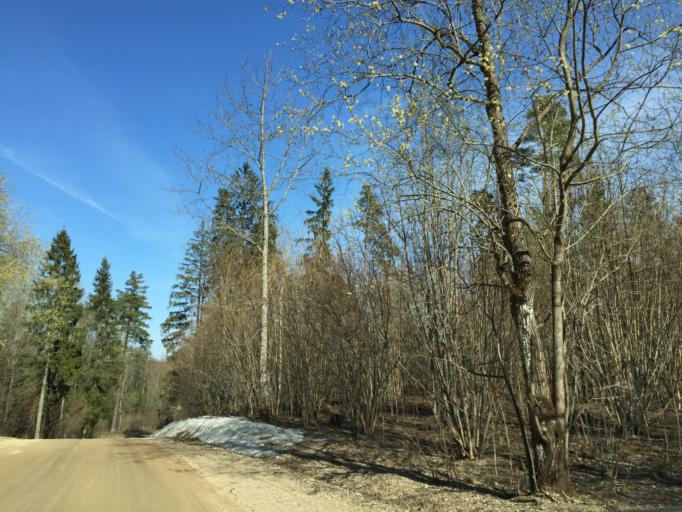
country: EE
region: Vorumaa
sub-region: Antsla vald
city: Vana-Antsla
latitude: 57.9943
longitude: 26.3769
